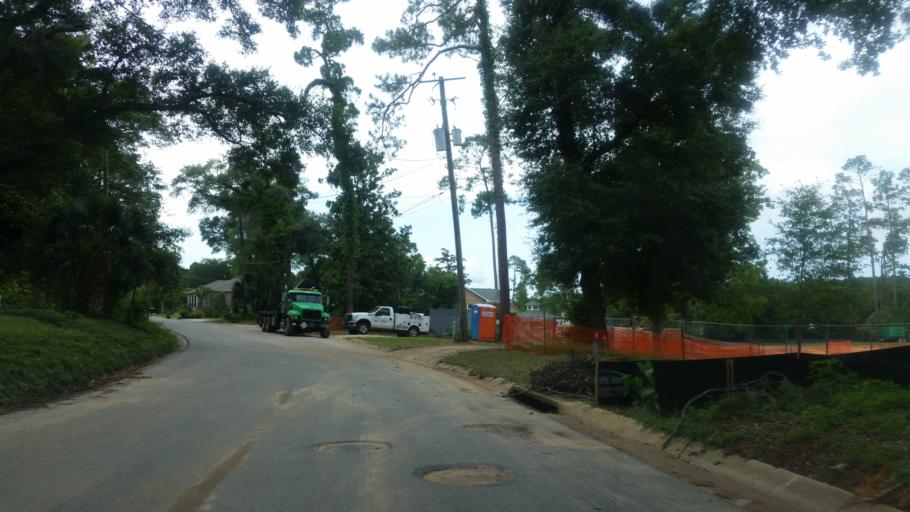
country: US
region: Florida
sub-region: Escambia County
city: Goulding
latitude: 30.4513
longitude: -87.2032
